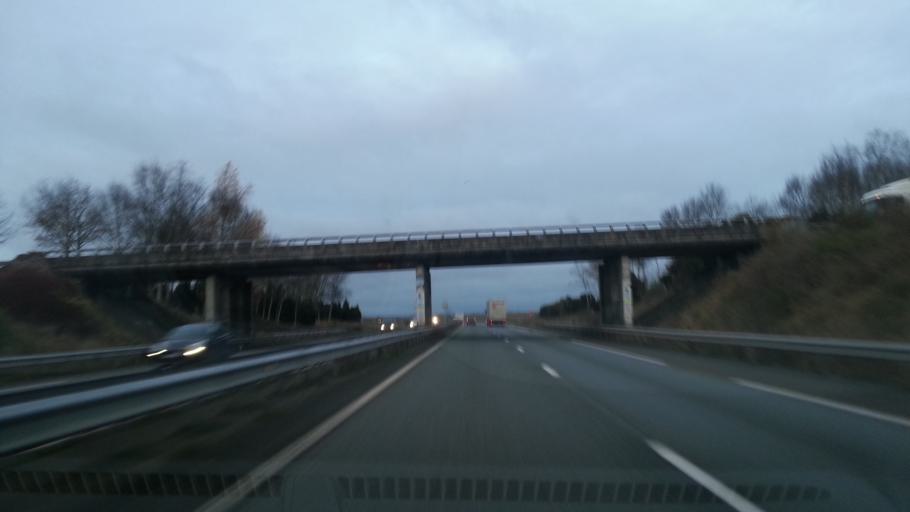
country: FR
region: Picardie
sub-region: Departement de l'Oise
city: Bresles
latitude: 49.4145
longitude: 2.3038
